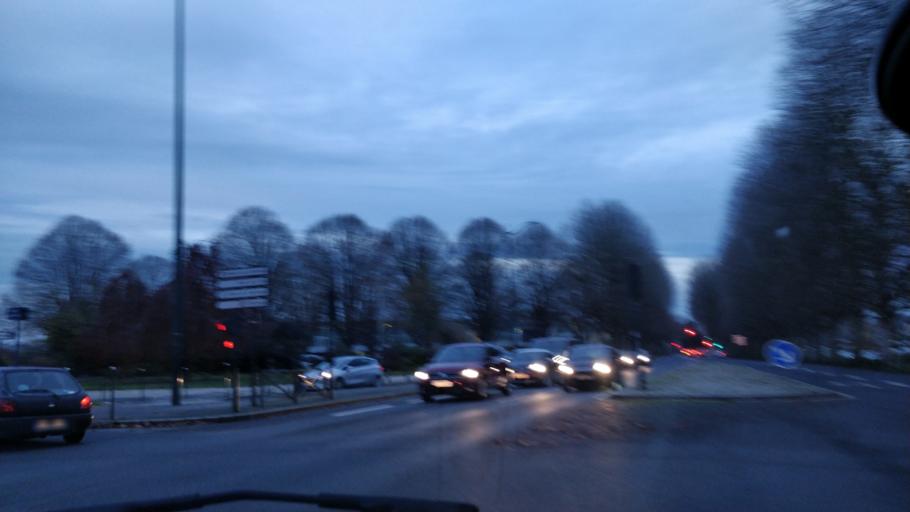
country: FR
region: Lower Normandy
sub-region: Departement du Calvados
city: Caen
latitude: 49.1751
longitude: -0.3709
